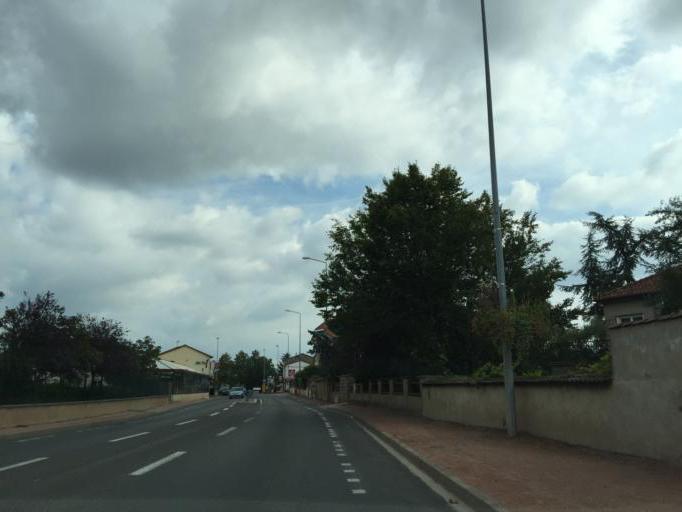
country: FR
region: Rhone-Alpes
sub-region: Departement de la Loire
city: Bonson
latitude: 45.5238
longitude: 4.2133
